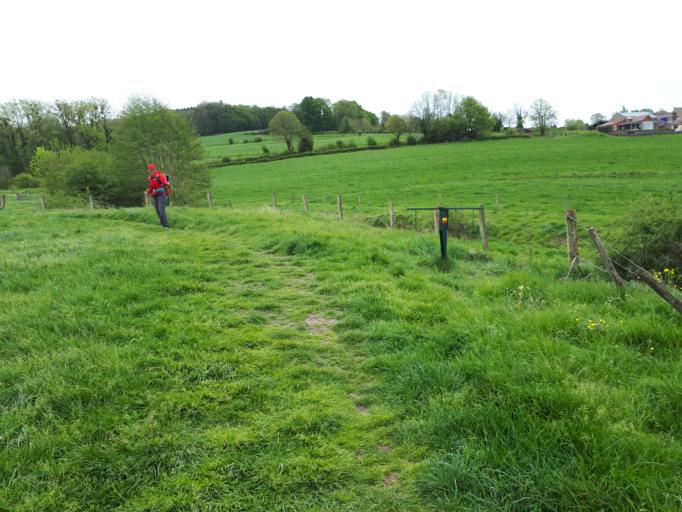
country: BE
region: Wallonia
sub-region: Province de Liege
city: Plombieres
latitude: 50.7753
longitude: 5.9243
